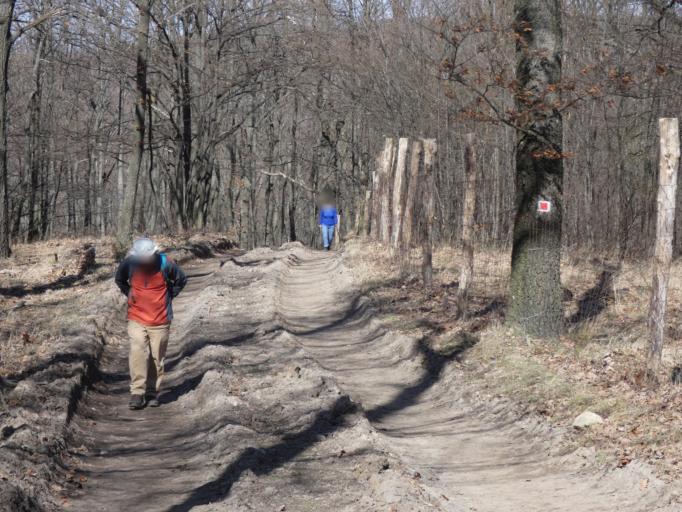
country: SK
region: Nitriansky
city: Sahy
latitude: 47.9846
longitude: 18.9570
